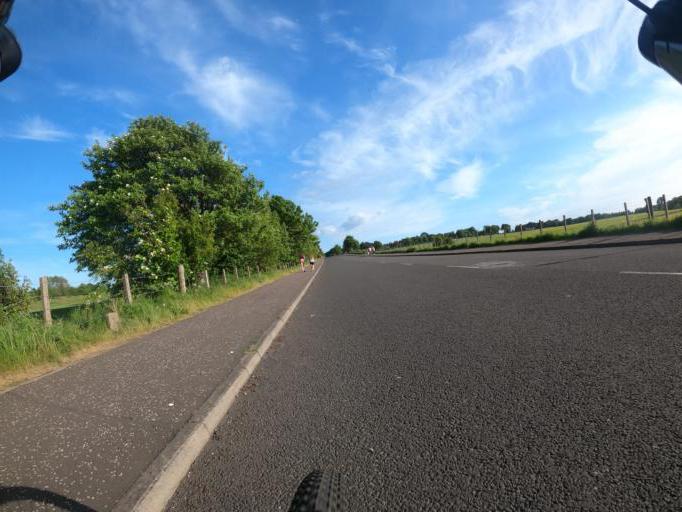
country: GB
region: Scotland
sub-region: Edinburgh
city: Colinton
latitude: 55.9781
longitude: -3.2783
